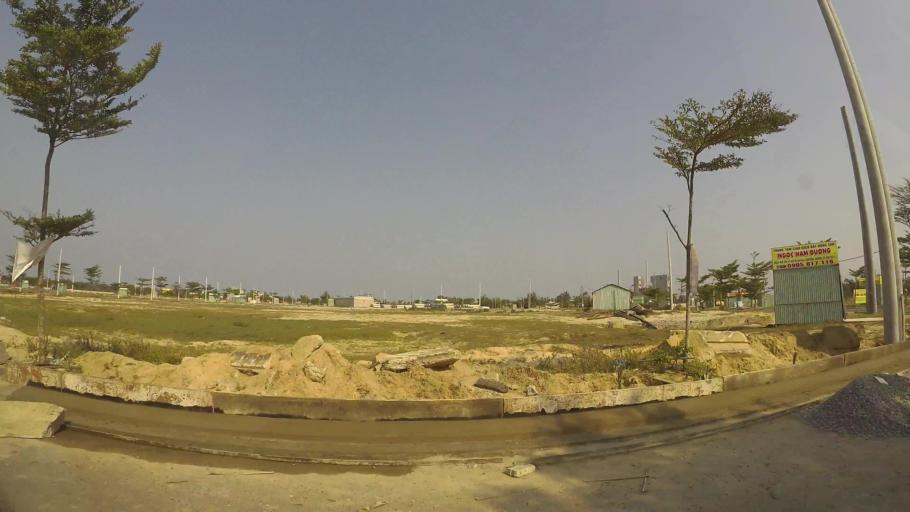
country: VN
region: Da Nang
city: Ngu Hanh Son
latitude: 15.9550
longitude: 108.2732
